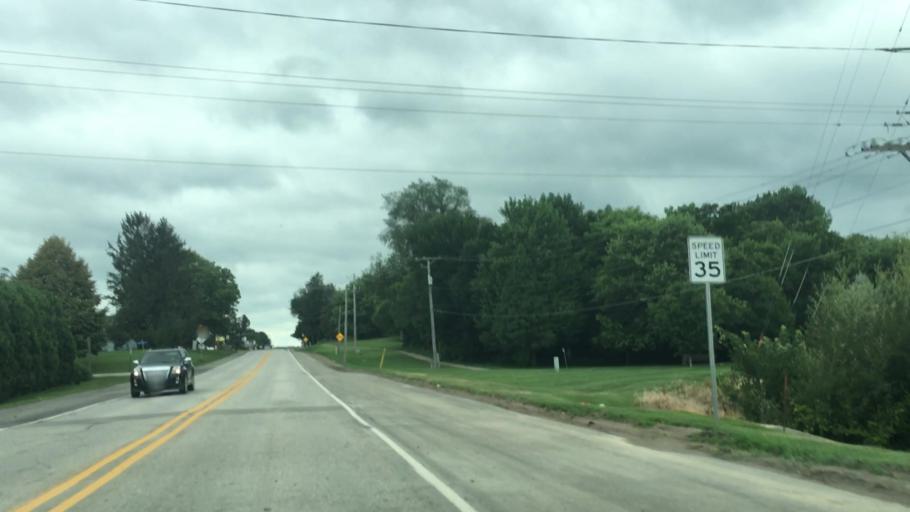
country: US
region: Iowa
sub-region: Johnson County
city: Tiffin
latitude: 41.7069
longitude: -91.6611
